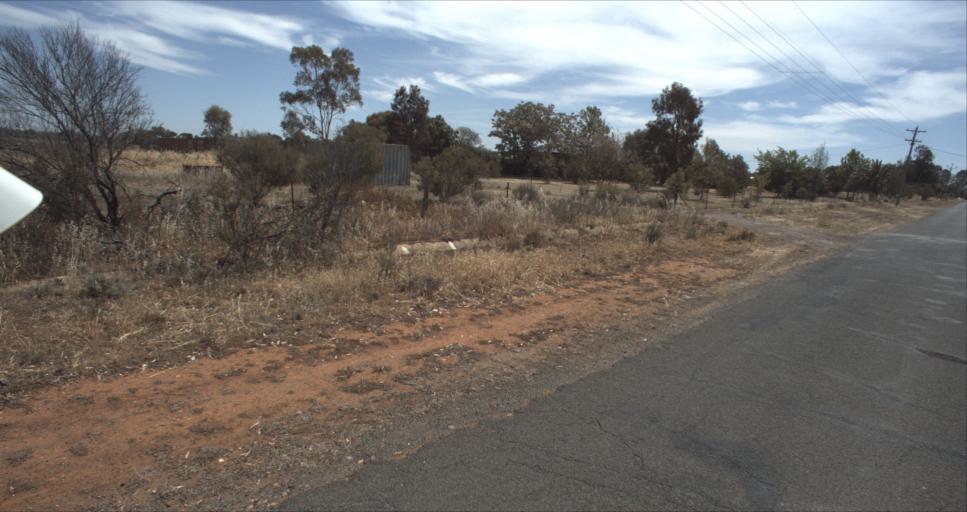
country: AU
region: New South Wales
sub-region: Leeton
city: Leeton
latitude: -34.5970
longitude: 146.4277
